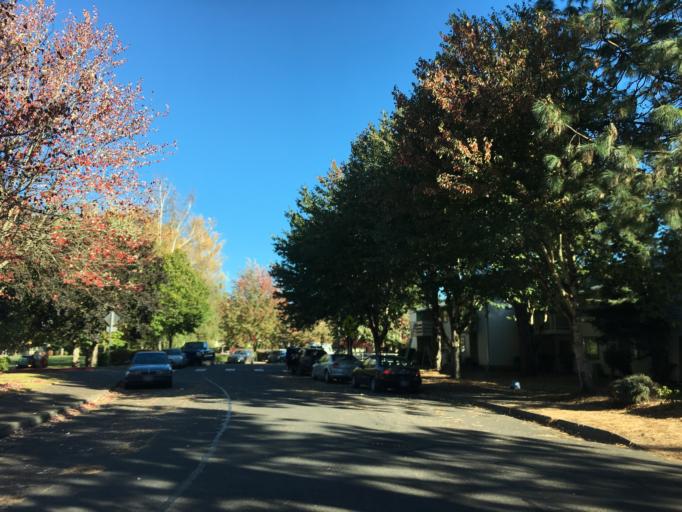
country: US
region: Oregon
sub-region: Multnomah County
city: Wood Village
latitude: 45.5140
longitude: -122.4144
